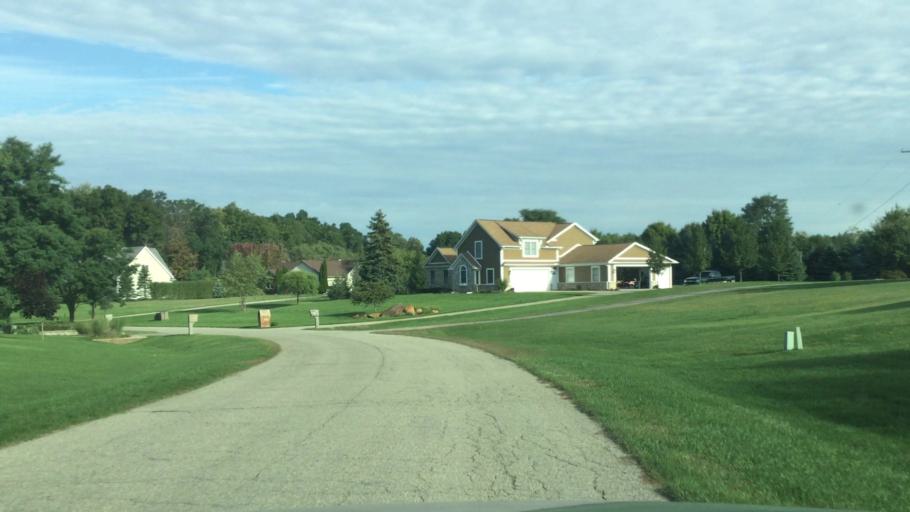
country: US
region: Michigan
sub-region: Livingston County
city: Howell
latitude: 42.6050
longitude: -83.8659
